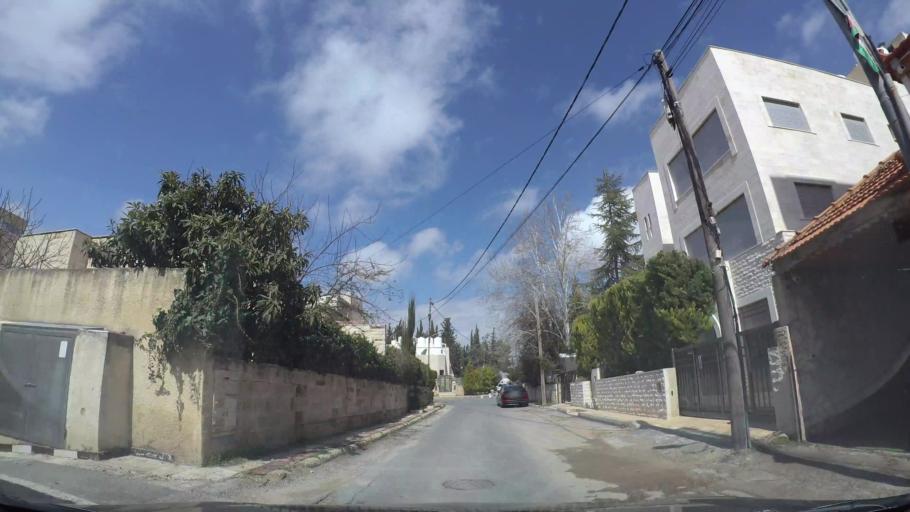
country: JO
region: Amman
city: Wadi as Sir
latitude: 31.9633
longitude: 35.8420
